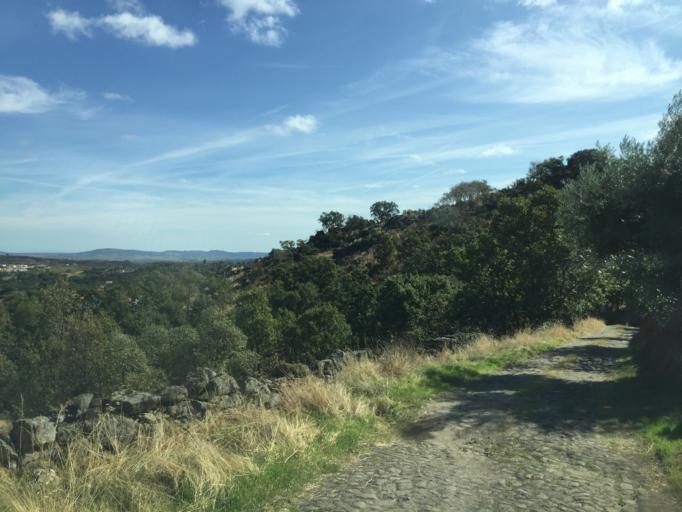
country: PT
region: Portalegre
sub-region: Marvao
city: Marvao
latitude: 39.4010
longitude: -7.3666
